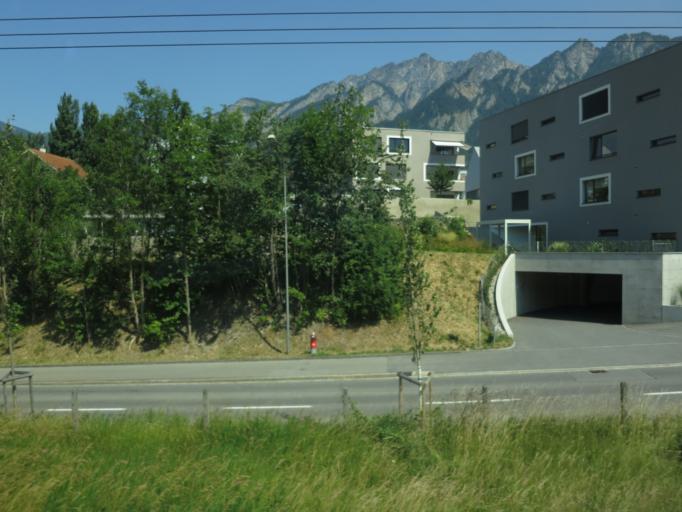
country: CH
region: Grisons
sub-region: Plessur District
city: Chur
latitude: 46.8730
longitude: 9.5328
